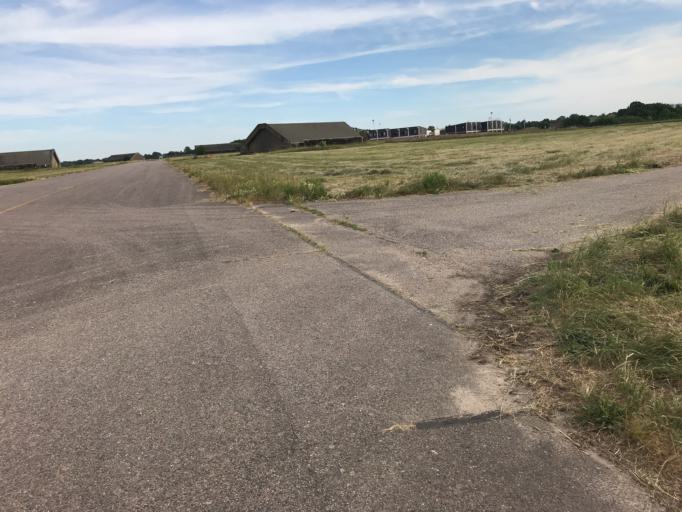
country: DK
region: Capital Region
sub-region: Ballerup Kommune
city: Malov
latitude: 55.7686
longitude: 12.3058
